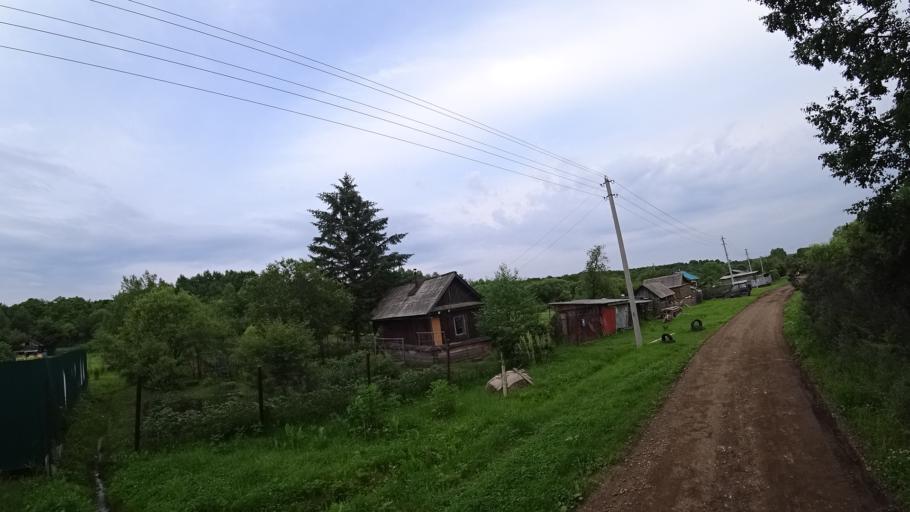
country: RU
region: Primorskiy
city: Novosysoyevka
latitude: 44.2379
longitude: 133.3790
